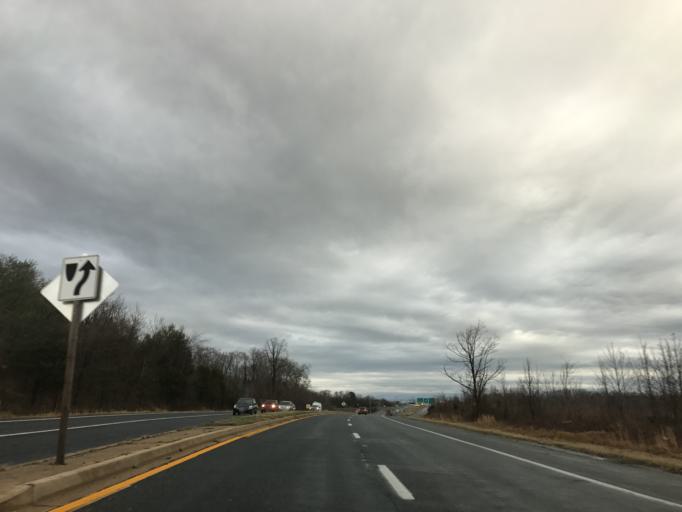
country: US
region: Maryland
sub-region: Harford County
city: Riverside
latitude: 39.4891
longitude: -76.2551
